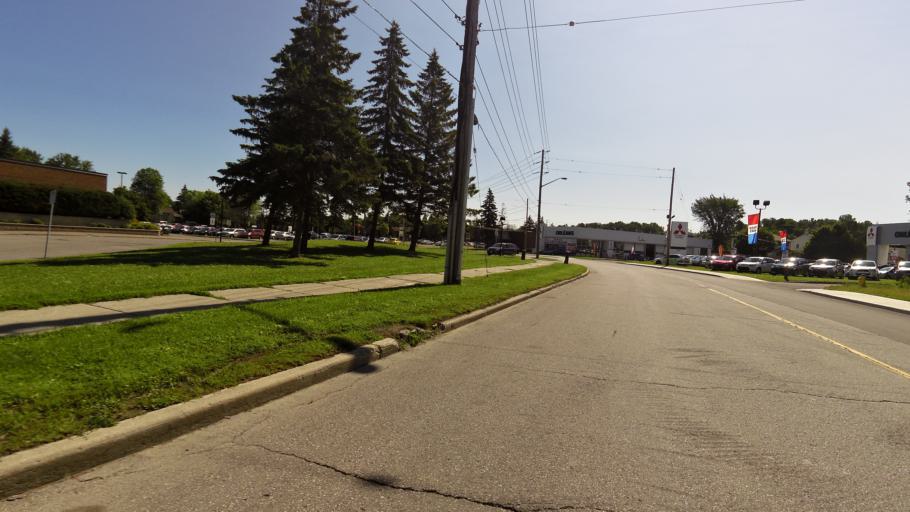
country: CA
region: Quebec
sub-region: Outaouais
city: Gatineau
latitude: 45.4654
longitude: -75.5445
